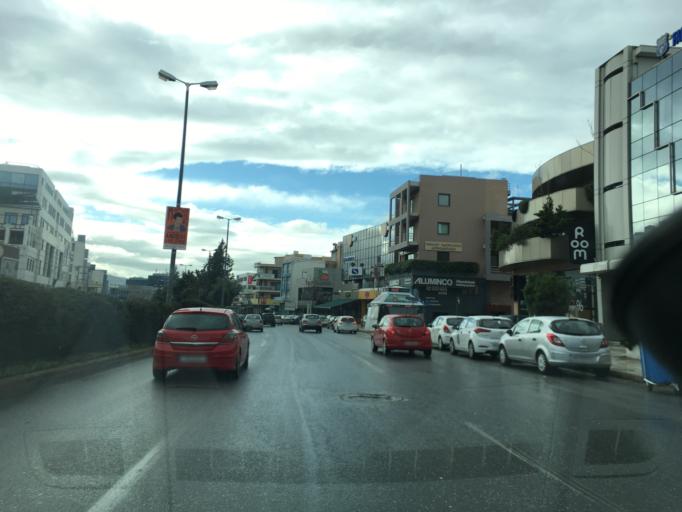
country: GR
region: Attica
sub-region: Nomarchia Athinas
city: Marousi
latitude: 38.0496
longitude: 23.8084
